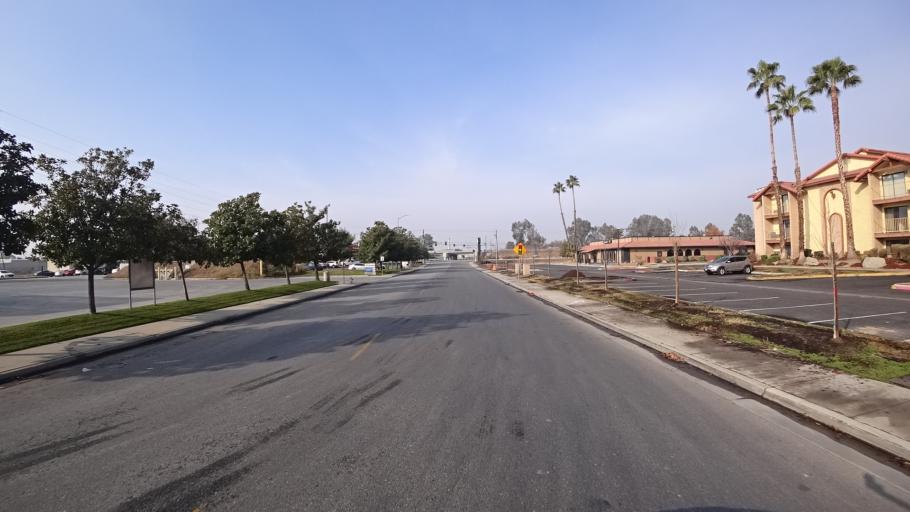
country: US
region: California
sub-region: Kern County
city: Oildale
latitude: 35.3986
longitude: -119.0417
